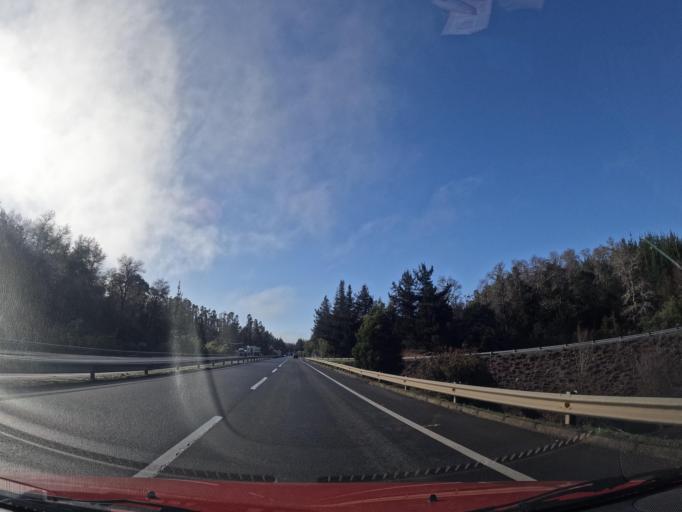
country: CL
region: Biobio
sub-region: Provincia de Concepcion
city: Penco
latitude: -36.7300
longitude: -72.8641
